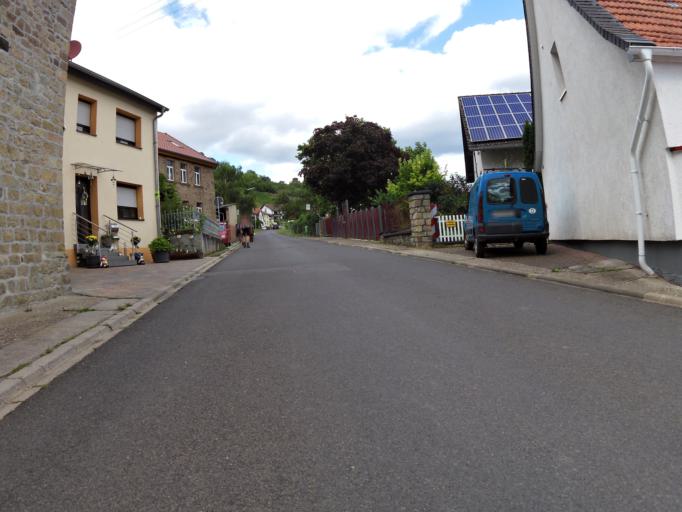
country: DE
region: Rheinland-Pfalz
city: Niederhausen
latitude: 49.8033
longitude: 7.7809
